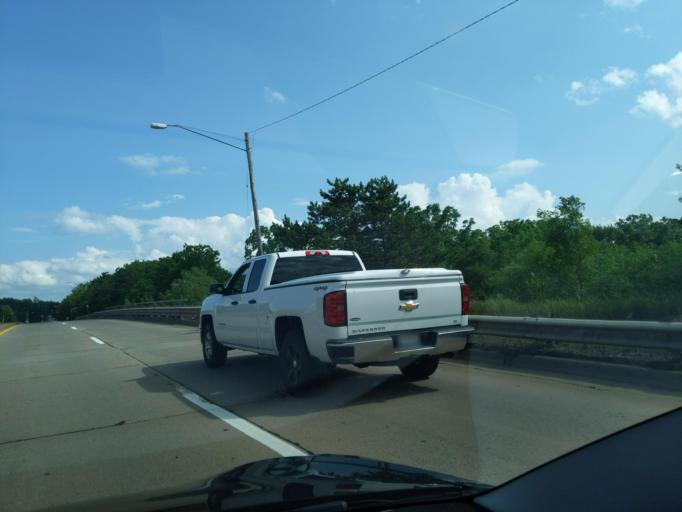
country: US
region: Michigan
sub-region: Jackson County
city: Jackson
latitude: 42.2367
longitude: -84.3956
